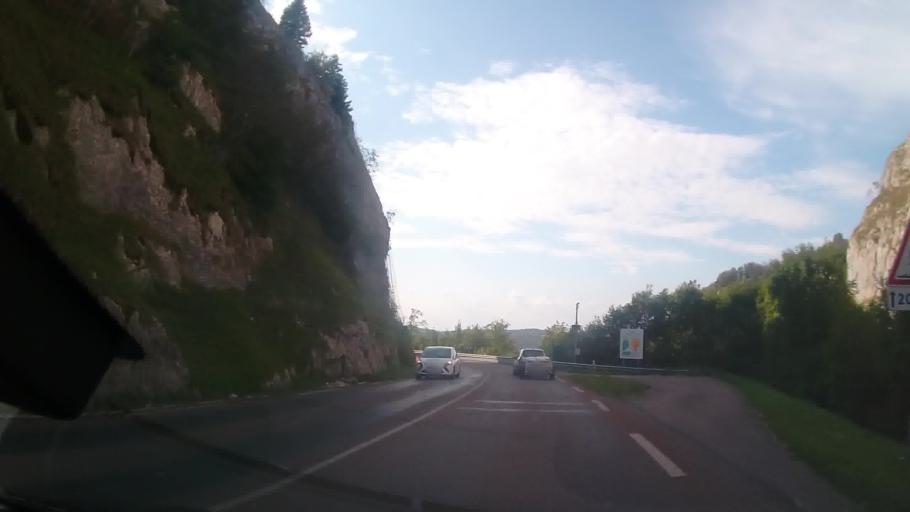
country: FR
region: Franche-Comte
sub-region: Departement du Jura
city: Morbier
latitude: 46.6093
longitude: 5.9028
